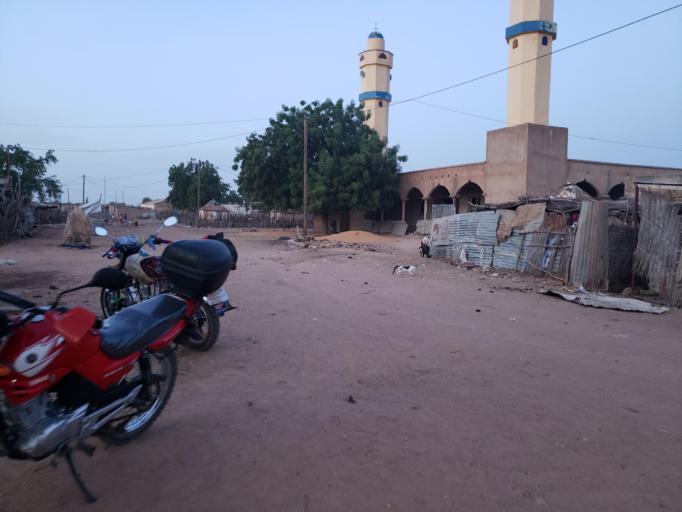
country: SN
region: Matam
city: Ranerou
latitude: 15.2984
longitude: -13.9598
